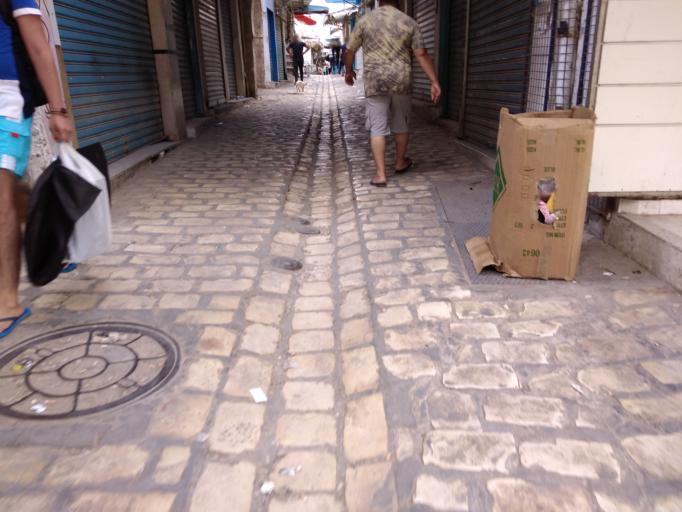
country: TN
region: Safaqis
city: Sfax
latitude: 34.7365
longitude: 10.7612
